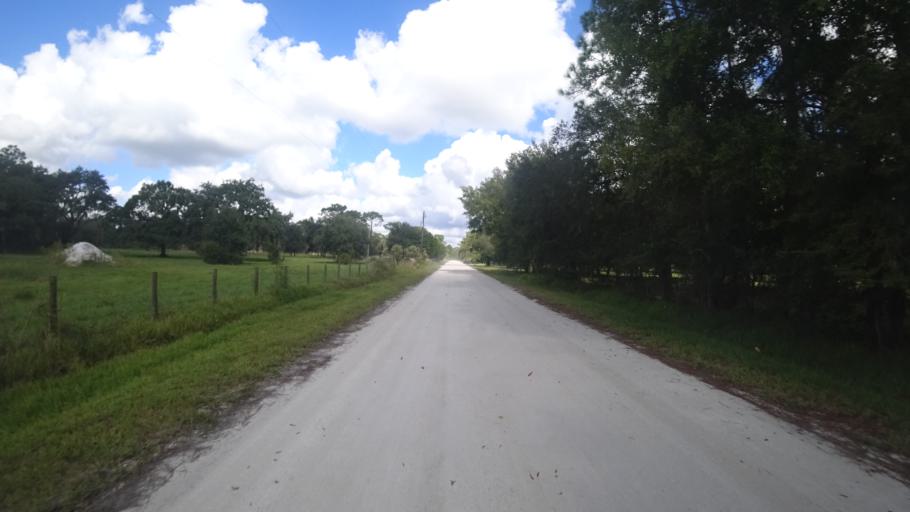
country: US
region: Florida
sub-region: Sarasota County
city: Lake Sarasota
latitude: 27.3796
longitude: -82.2194
